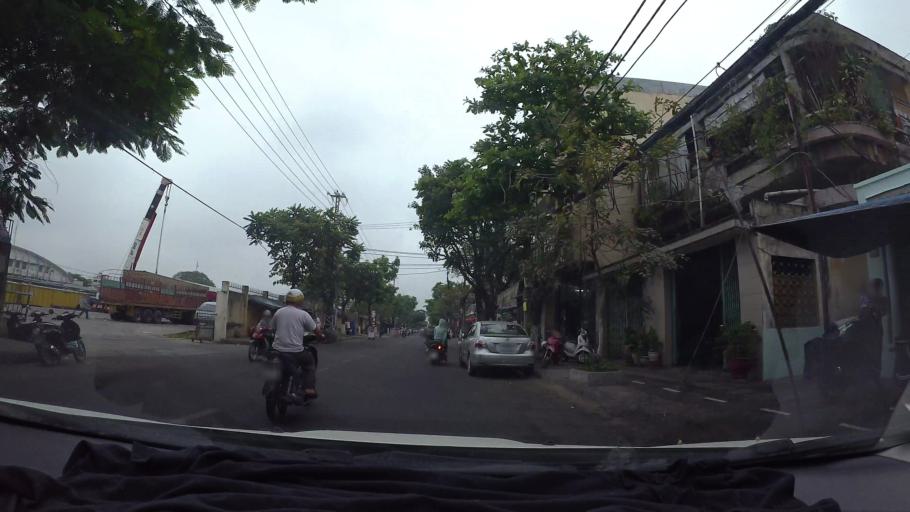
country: VN
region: Da Nang
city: Da Nang
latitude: 16.0728
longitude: 108.2098
